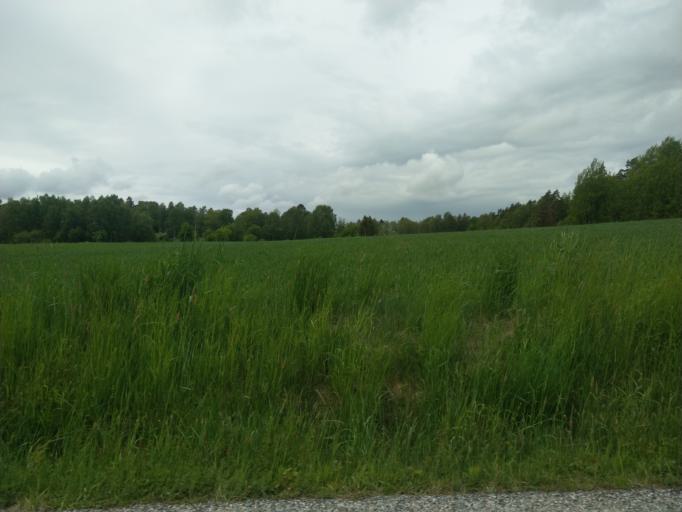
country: SE
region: Stockholm
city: Stenhamra
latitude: 59.4142
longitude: 17.6168
